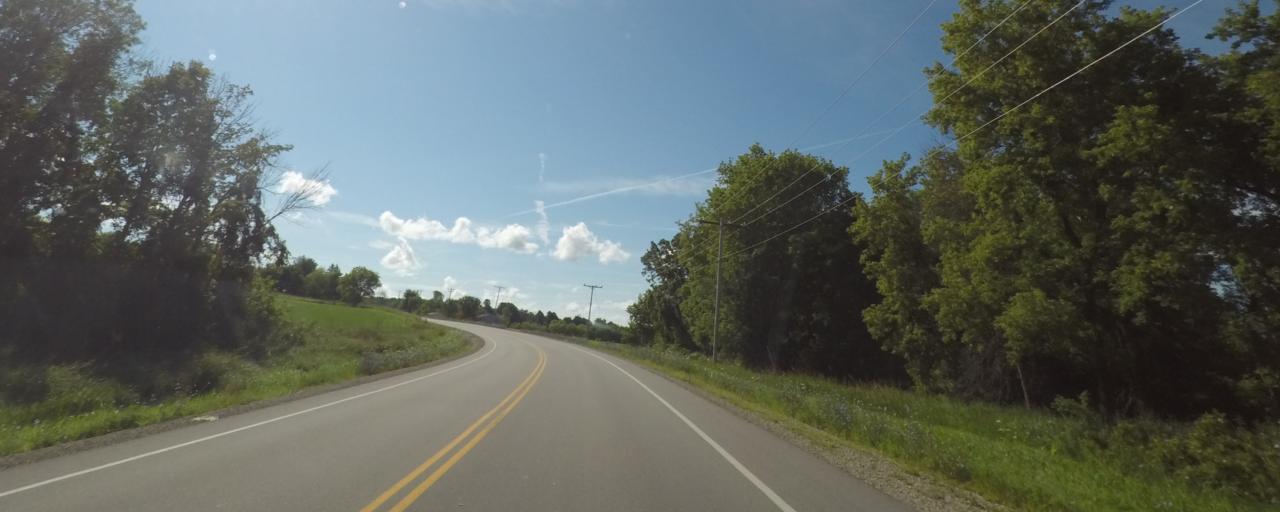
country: US
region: Wisconsin
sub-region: Jefferson County
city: Ixonia
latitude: 43.0703
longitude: -88.6348
